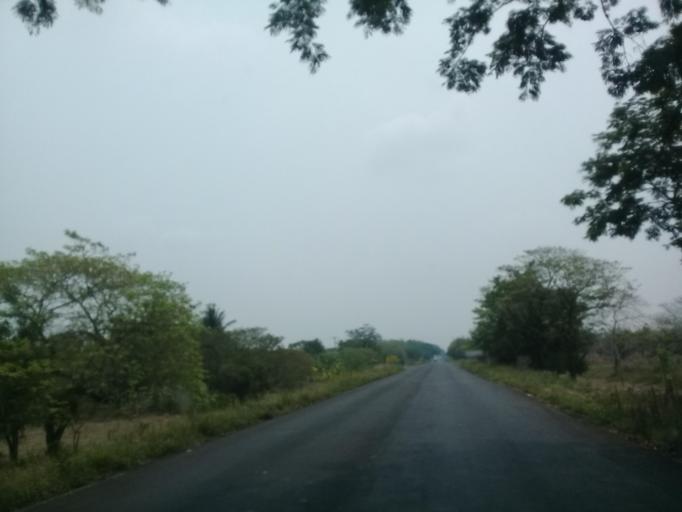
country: MX
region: Veracruz
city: Paso del Toro
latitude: 18.9571
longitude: -96.1932
